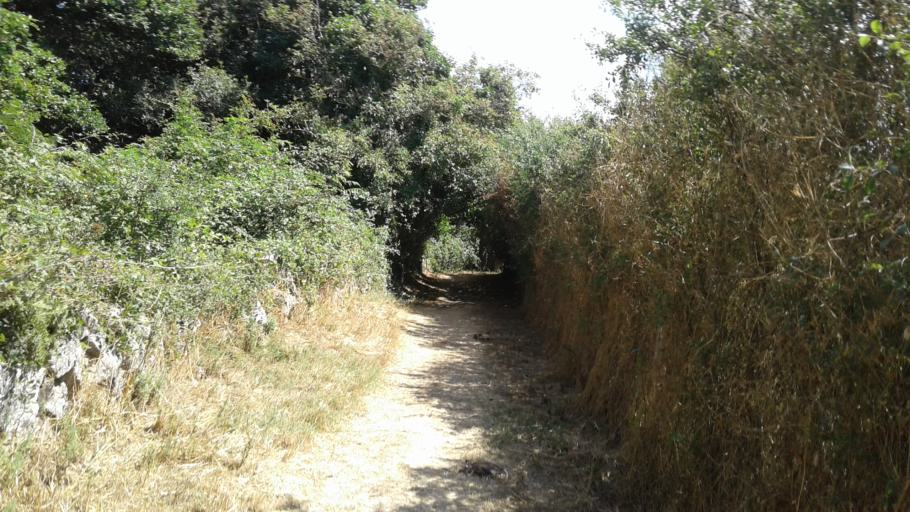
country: IT
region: Sardinia
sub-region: Provincia di Olbia-Tempio
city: Calangianus
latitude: 40.9088
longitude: 9.1721
